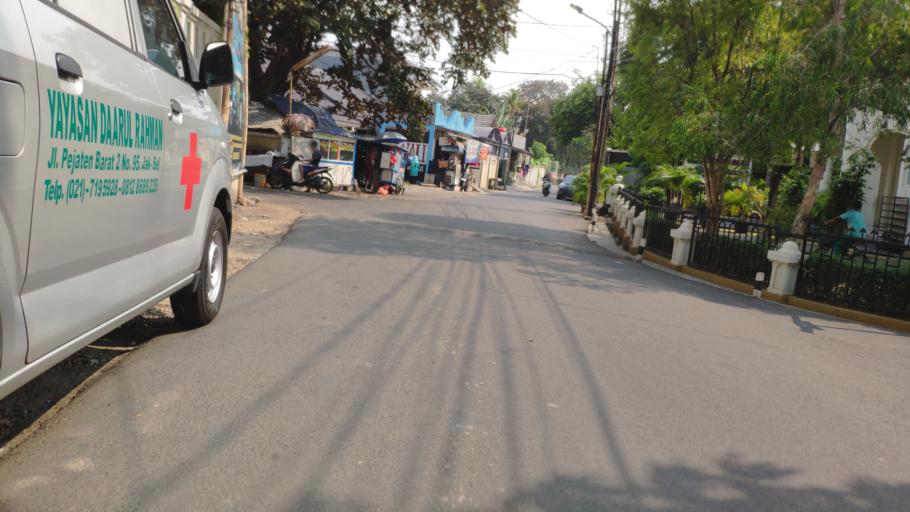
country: ID
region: Jakarta Raya
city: Jakarta
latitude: -6.2727
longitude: 106.8255
